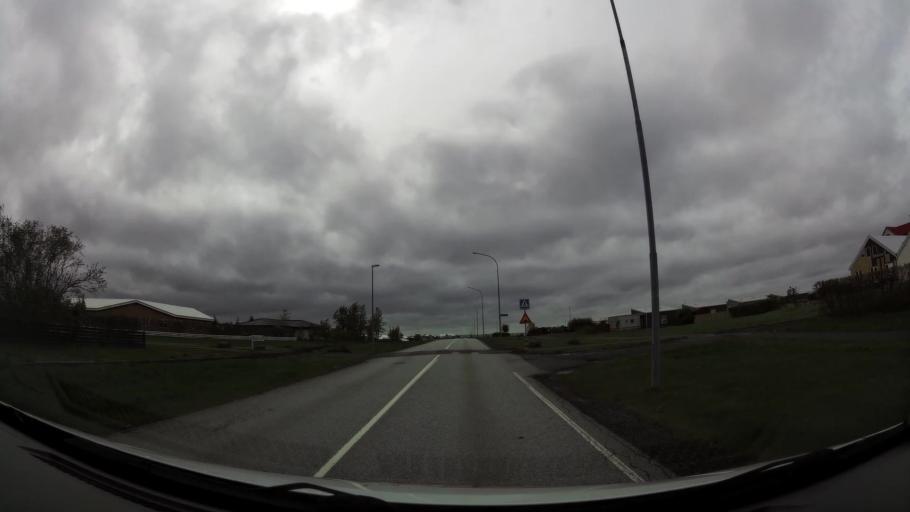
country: IS
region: Capital Region
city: Alftanes
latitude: 64.1093
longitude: -22.0184
